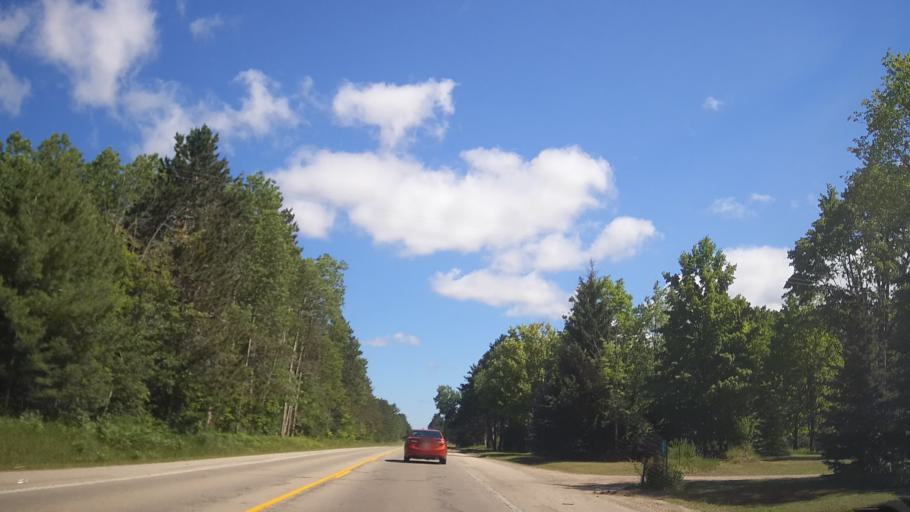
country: US
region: Michigan
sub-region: Cheboygan County
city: Indian River
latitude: 45.4585
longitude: -84.7832
